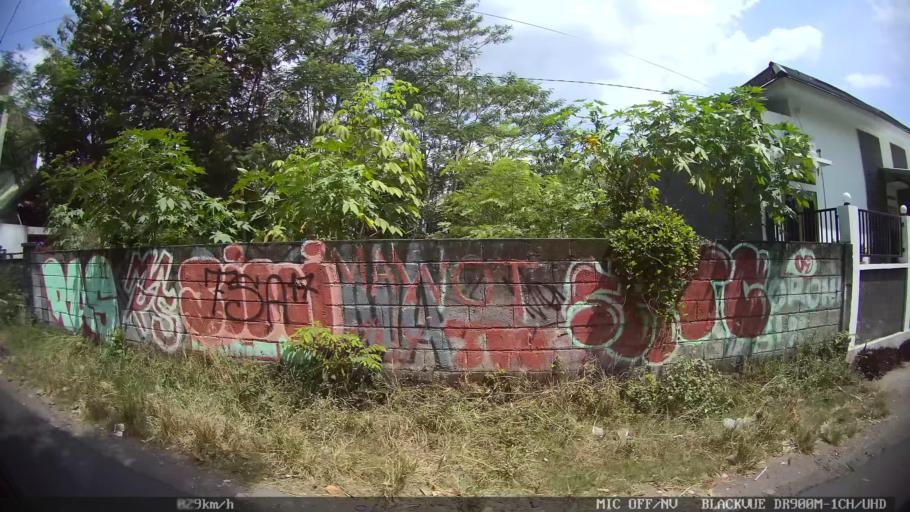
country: ID
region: Daerah Istimewa Yogyakarta
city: Kasihan
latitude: -7.8129
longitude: 110.3395
